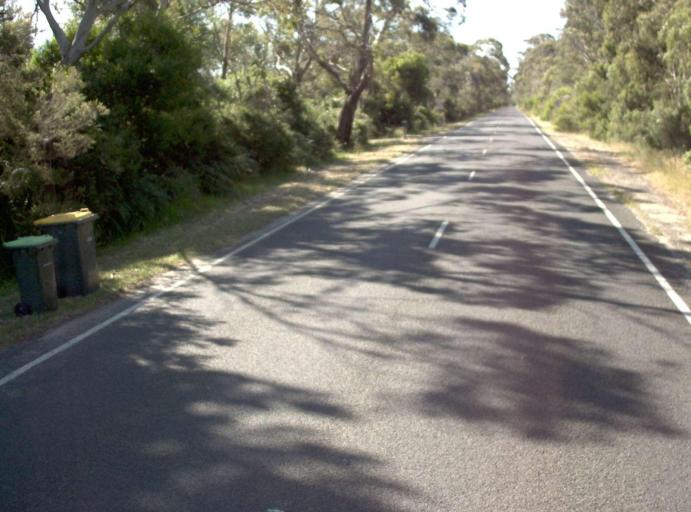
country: AU
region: Victoria
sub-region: Latrobe
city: Traralgon
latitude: -38.6619
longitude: 146.6847
